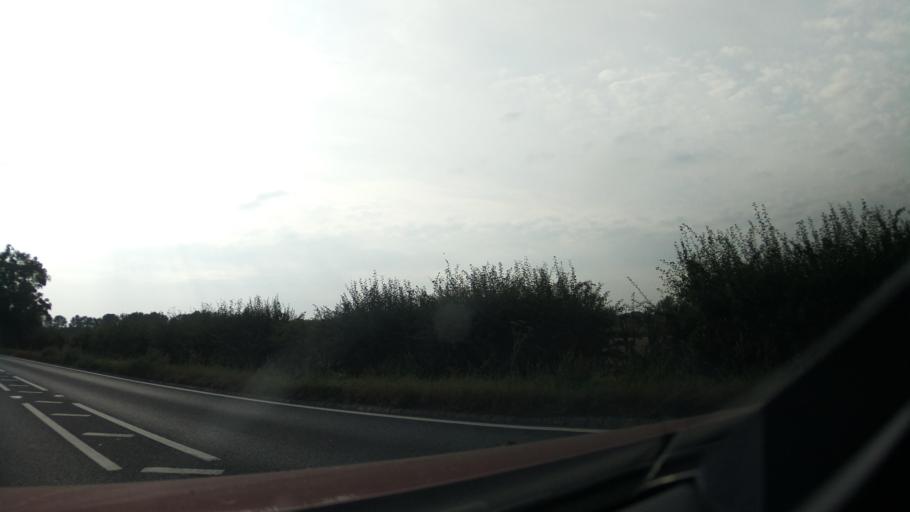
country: GB
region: England
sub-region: Gloucestershire
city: Gotherington
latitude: 52.0212
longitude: -2.0175
